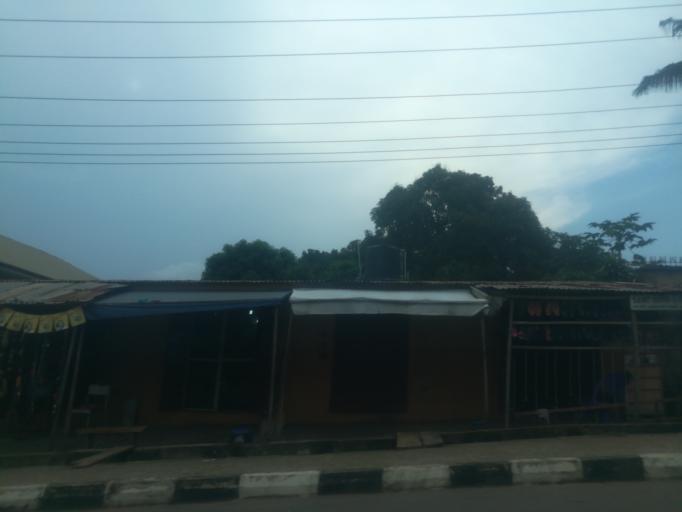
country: NG
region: Oyo
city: Ibadan
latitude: 7.3788
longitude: 3.8288
